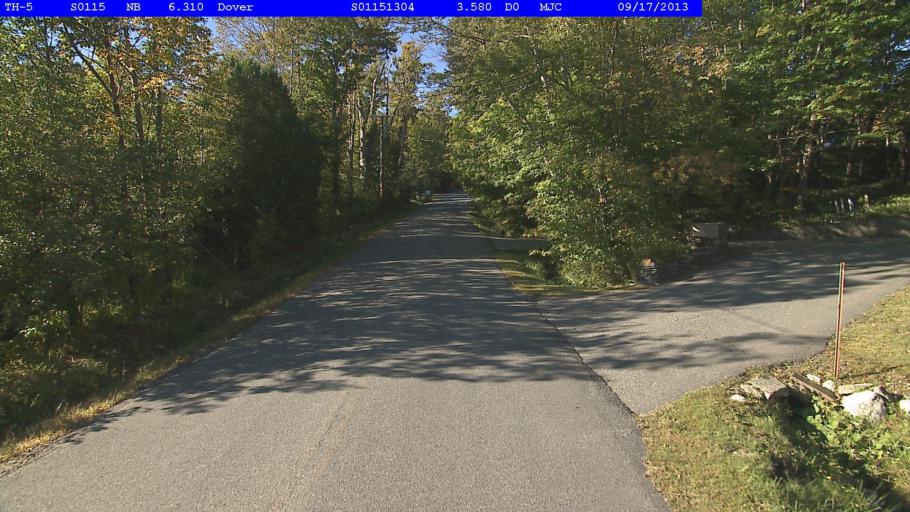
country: US
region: Vermont
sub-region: Windham County
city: Dover
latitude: 42.9749
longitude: -72.8924
